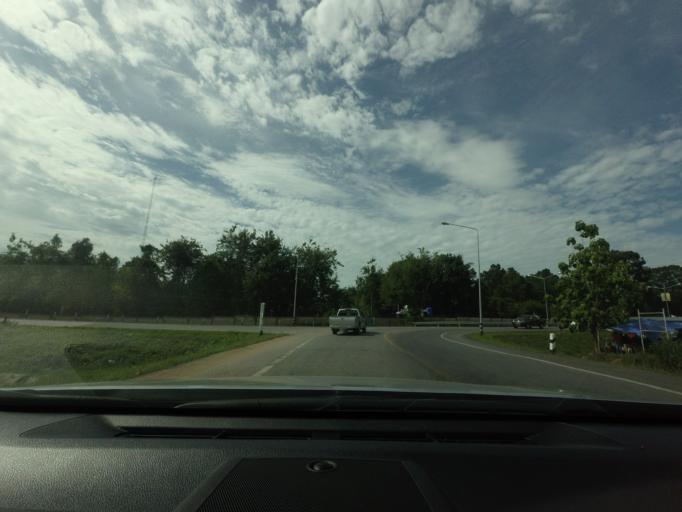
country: TH
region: Songkhla
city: Khlong Hoi Khong
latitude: 6.9228
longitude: 100.4109
